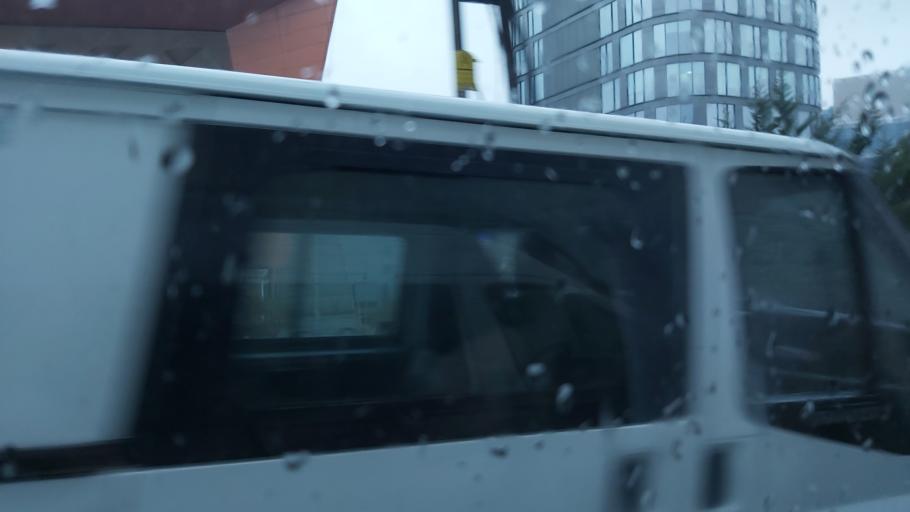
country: TR
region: Istanbul
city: Sisli
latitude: 41.0867
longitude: 28.9835
